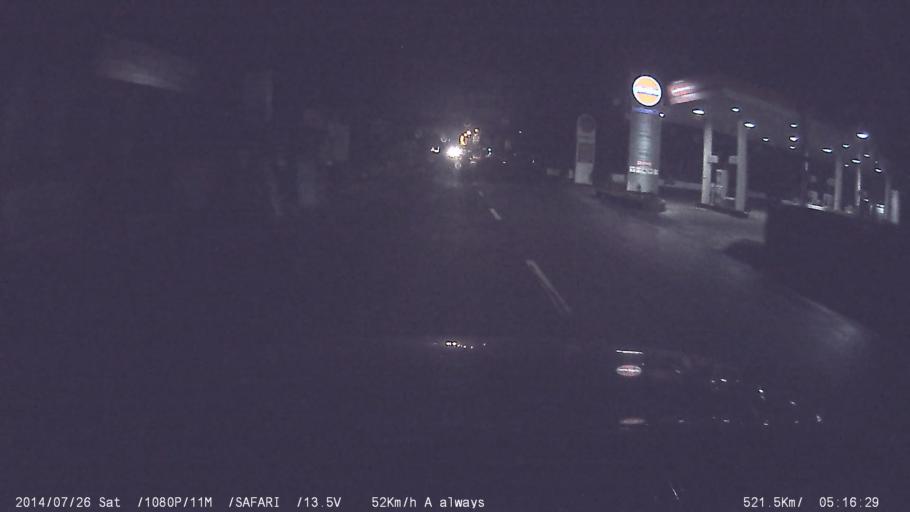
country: IN
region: Kerala
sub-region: Ernakulam
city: Muvattupula
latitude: 10.0206
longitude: 76.5603
